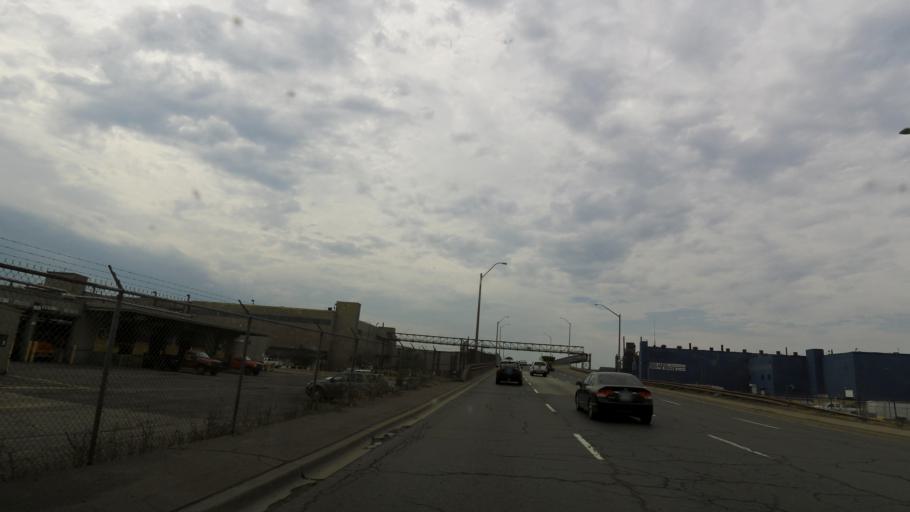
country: CA
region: Ontario
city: Hamilton
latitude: 43.2636
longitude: -79.8170
